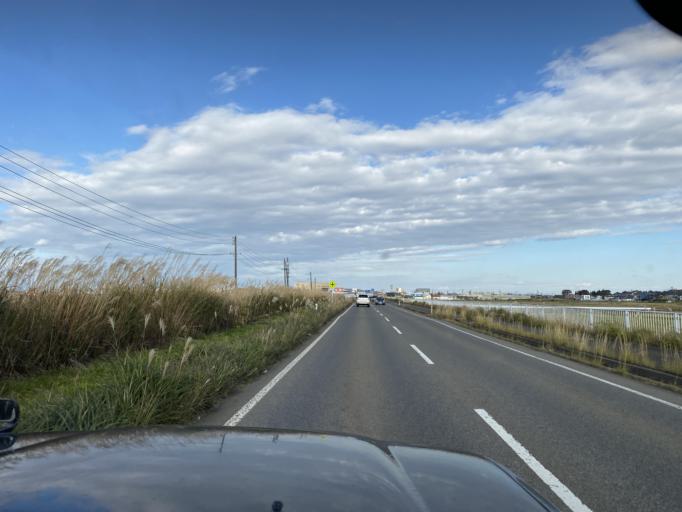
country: JP
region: Niigata
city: Niitsu-honcho
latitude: 37.7799
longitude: 139.1094
